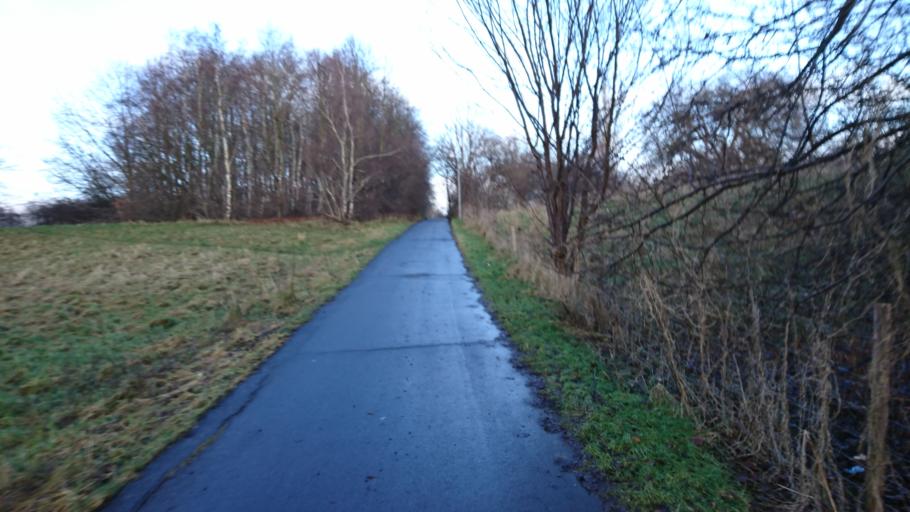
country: DK
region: Capital Region
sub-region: Ballerup Kommune
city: Ballerup
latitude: 55.7424
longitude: 12.3768
